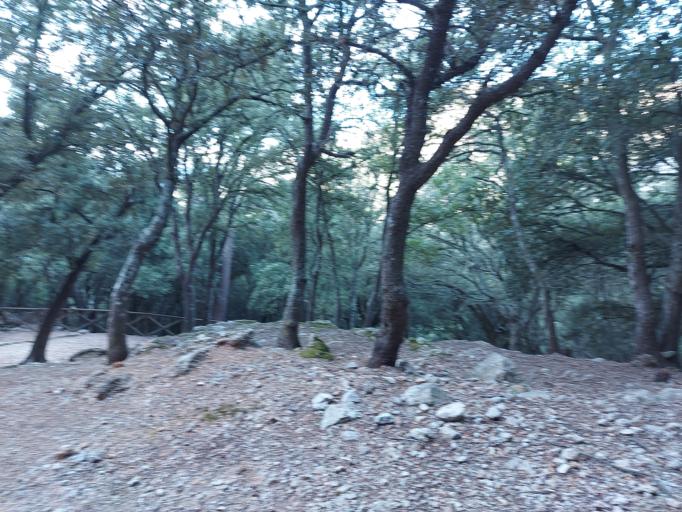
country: ES
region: Balearic Islands
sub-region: Illes Balears
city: Deia
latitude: 39.7272
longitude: 2.6542
